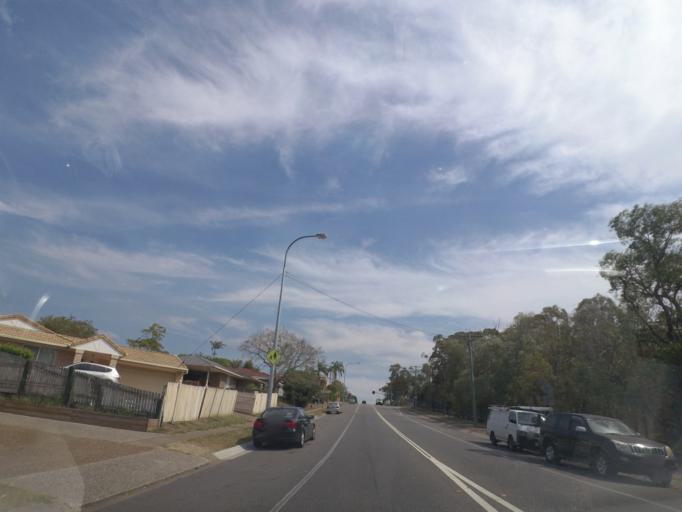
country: AU
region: Queensland
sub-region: Brisbane
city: Sunnybank Hills
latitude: -27.6020
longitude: 153.0638
